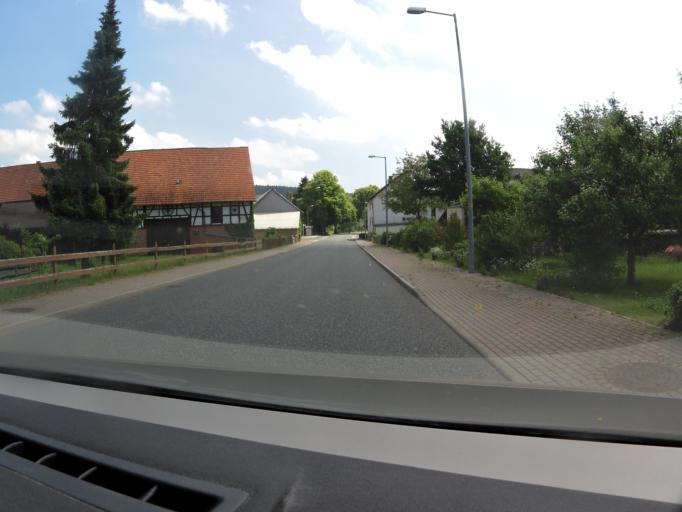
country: DE
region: Hesse
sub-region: Regierungsbezirk Kassel
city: Nentershausen
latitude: 50.9878
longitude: 9.9719
